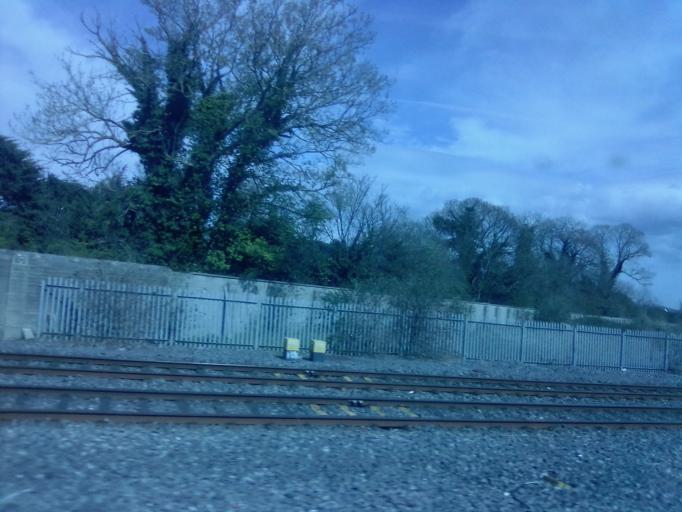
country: IE
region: Leinster
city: Clondalkin
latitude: 53.3330
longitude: -6.3993
